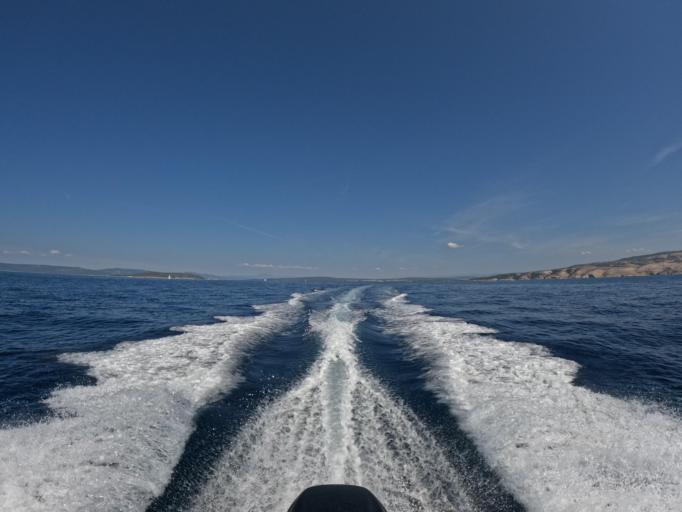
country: HR
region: Primorsko-Goranska
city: Punat
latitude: 44.9309
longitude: 14.6173
